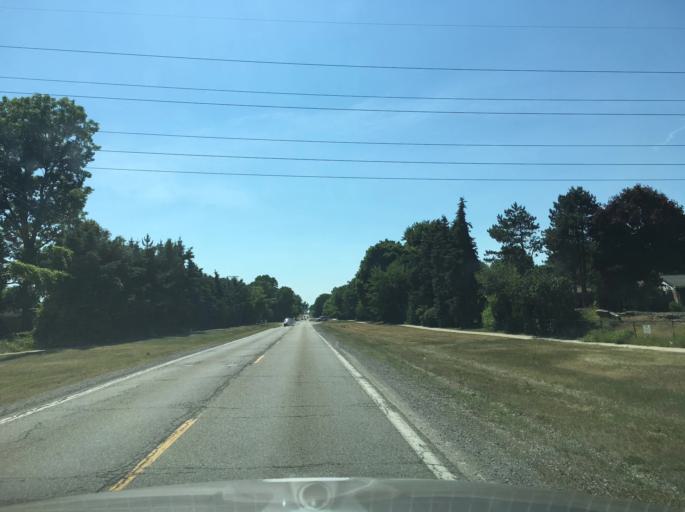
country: US
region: Michigan
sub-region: Macomb County
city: Utica
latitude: 42.6410
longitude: -83.0029
